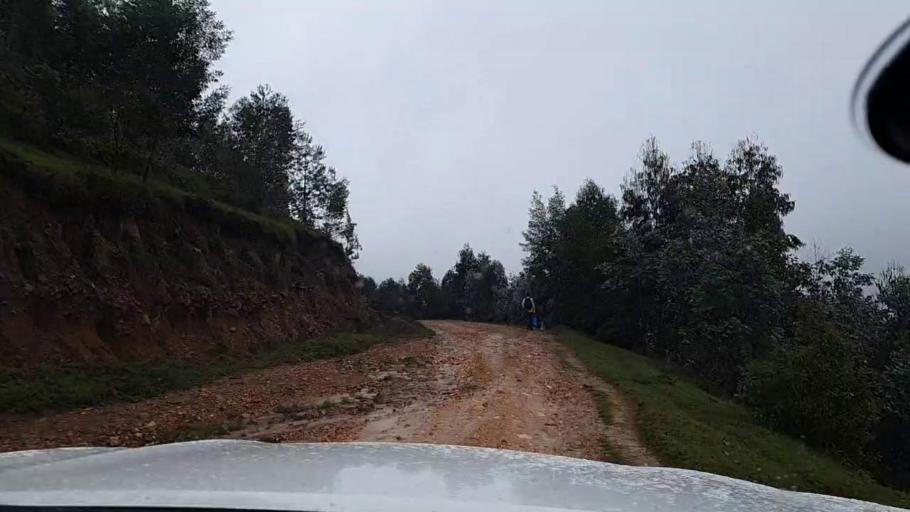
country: RW
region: Western Province
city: Kibuye
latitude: -2.1334
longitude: 29.4679
